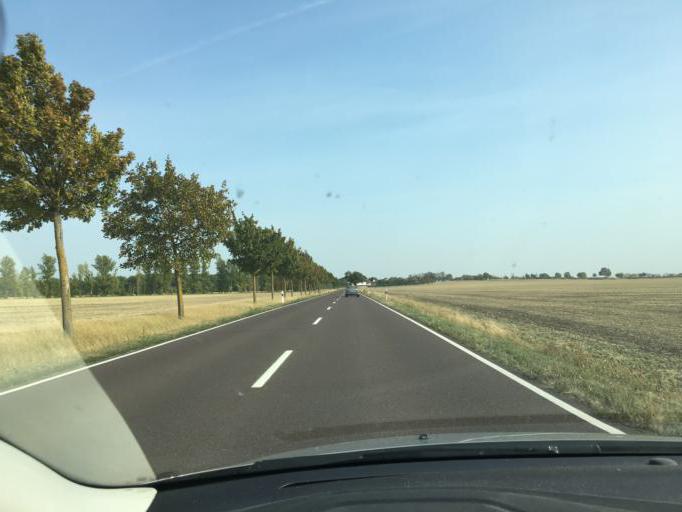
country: DE
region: Saxony-Anhalt
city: Wulfen
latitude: 51.7797
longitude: 11.8956
